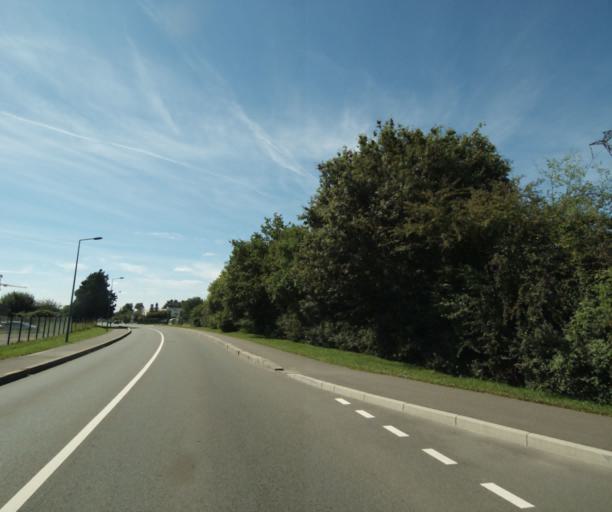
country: FR
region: Pays de la Loire
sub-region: Departement de la Mayenne
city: Saint-Berthevin
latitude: 48.0571
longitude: -0.8033
